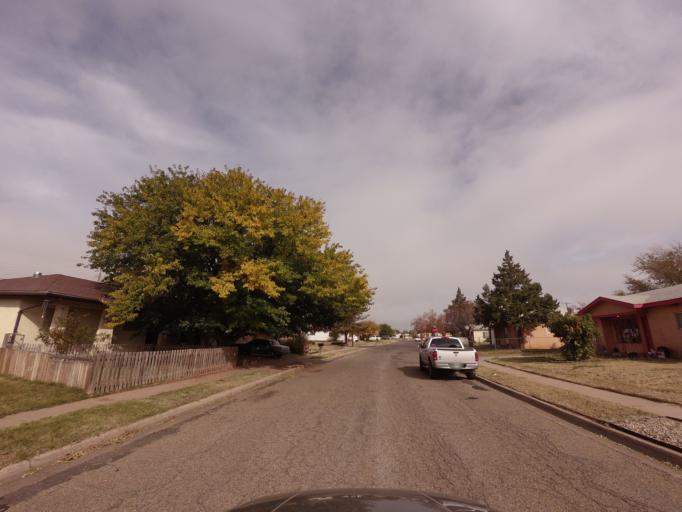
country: US
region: New Mexico
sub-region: Curry County
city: Clovis
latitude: 34.4265
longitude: -103.2171
